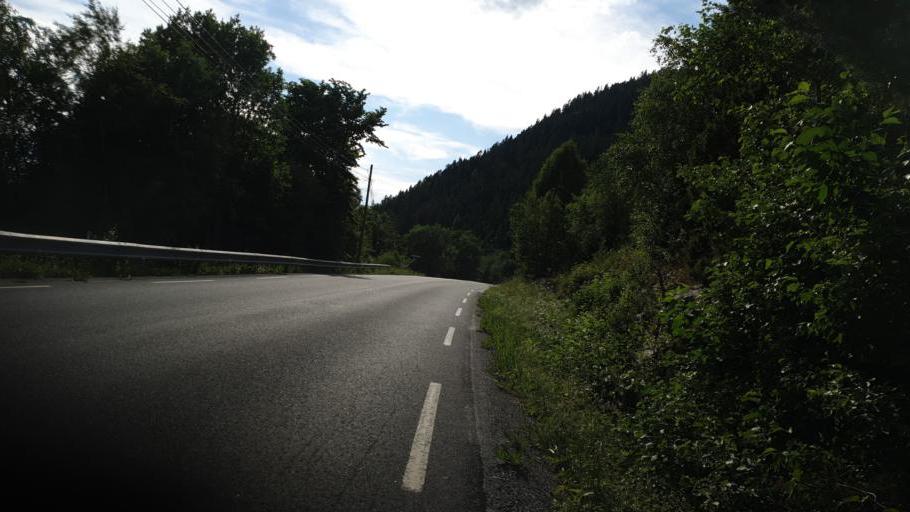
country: NO
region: Sor-Trondelag
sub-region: Trondheim
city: Trondheim
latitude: 63.5576
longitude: 10.2758
